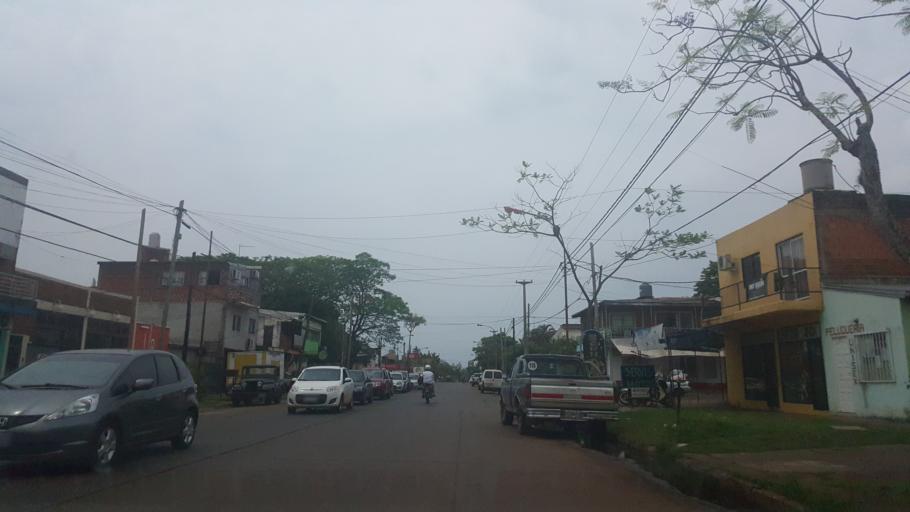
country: AR
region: Misiones
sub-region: Departamento de Capital
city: Posadas
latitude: -27.3690
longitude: -55.9160
